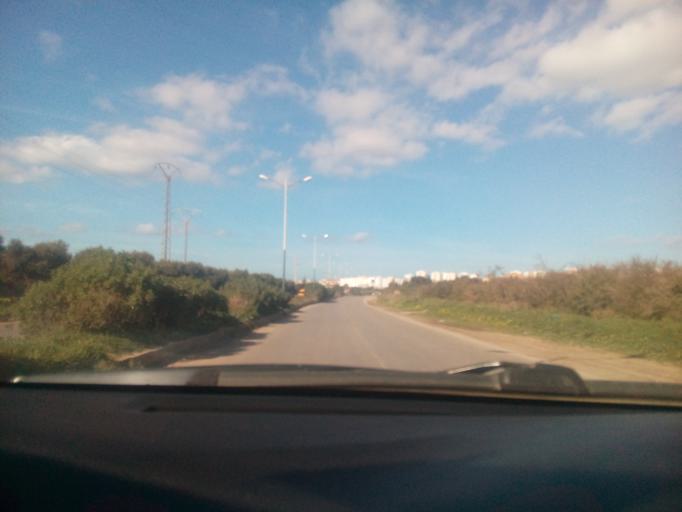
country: DZ
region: Oran
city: Bir el Djir
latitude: 35.6857
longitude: -0.5731
